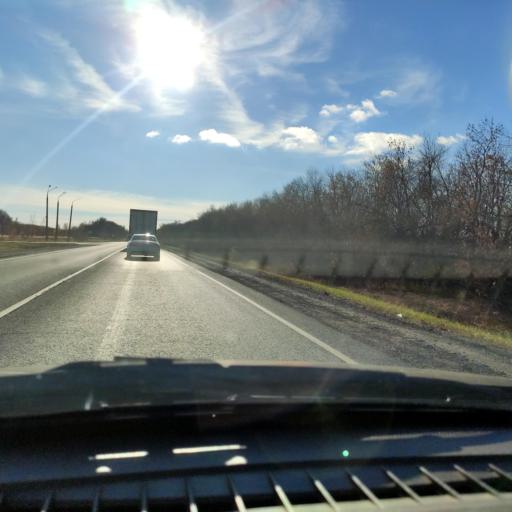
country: RU
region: Samara
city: Zhigulevsk
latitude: 53.3160
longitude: 49.3632
